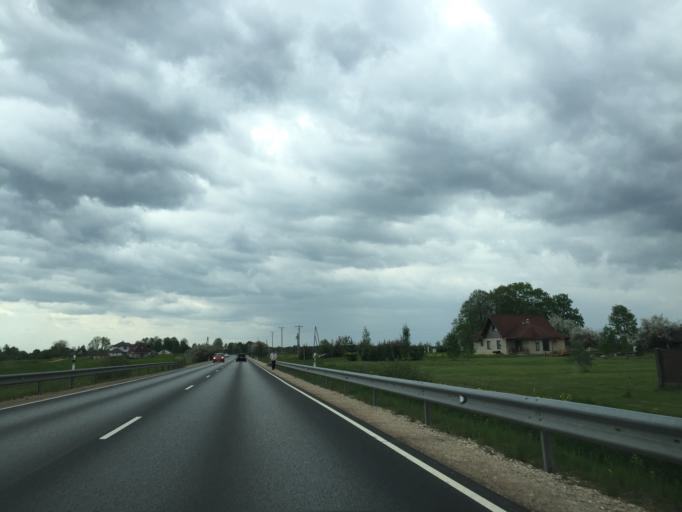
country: LV
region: Ikskile
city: Ikskile
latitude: 56.8691
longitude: 24.5465
